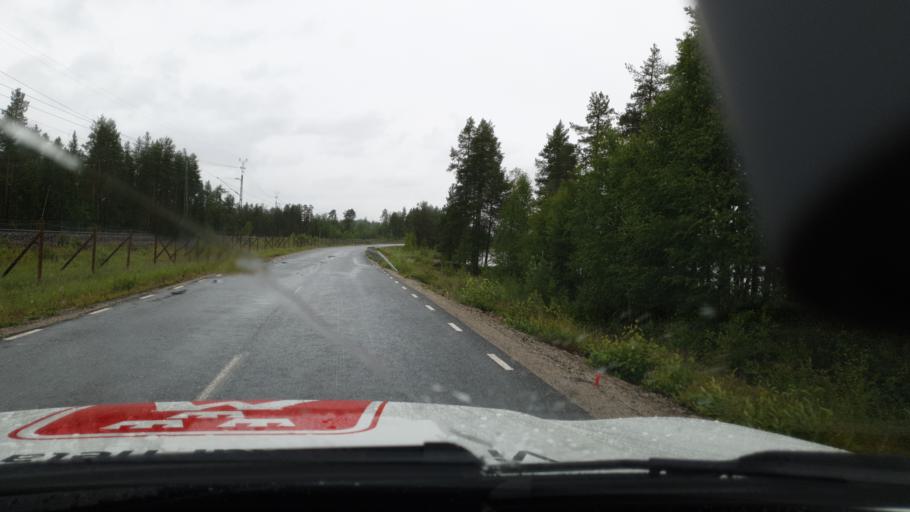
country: SE
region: Vaesterbotten
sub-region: Vindelns Kommun
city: Vindeln
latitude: 64.4492
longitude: 19.7481
